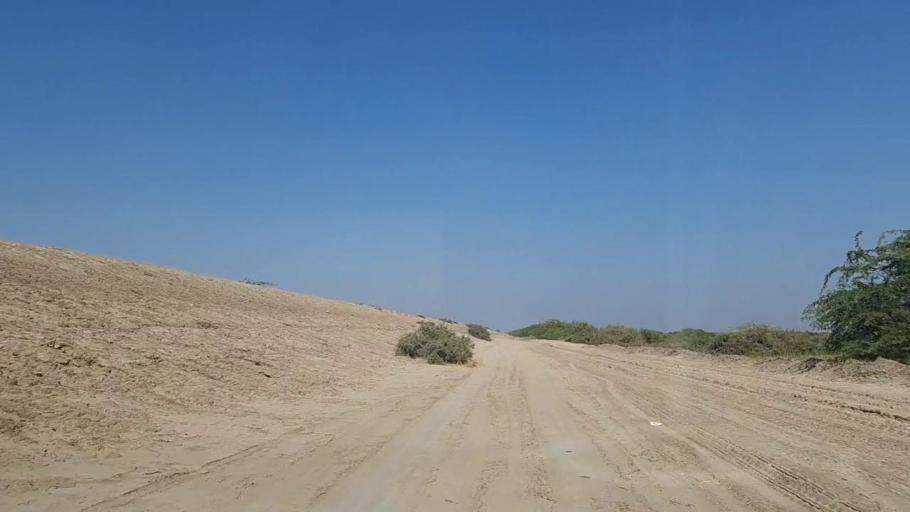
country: PK
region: Sindh
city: Chuhar Jamali
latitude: 24.4698
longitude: 68.0070
